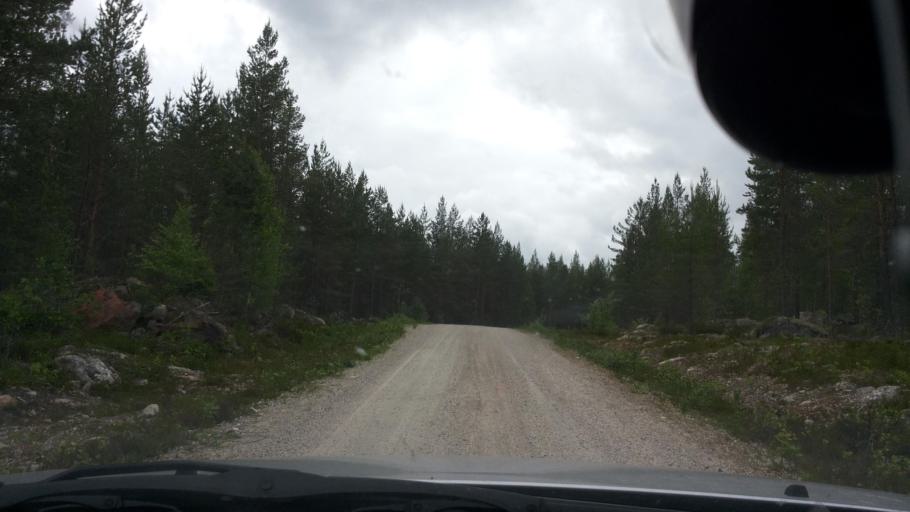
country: SE
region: Gaevleborg
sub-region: Ovanakers Kommun
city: Edsbyn
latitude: 61.4908
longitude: 15.3247
